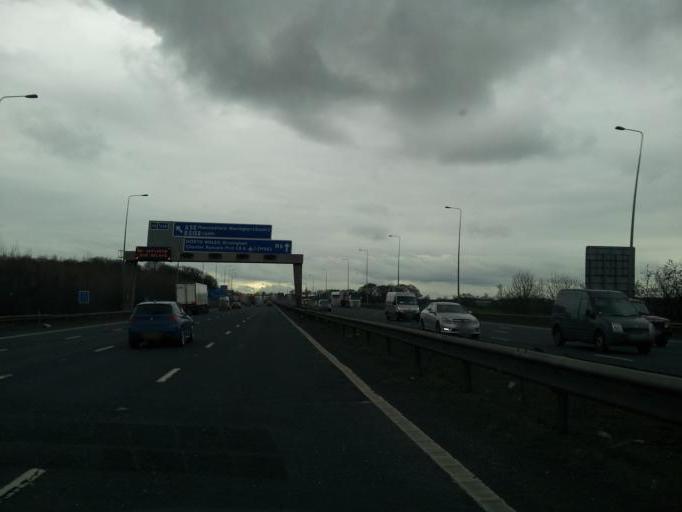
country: GB
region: England
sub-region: Warrington
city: Lymm
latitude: 53.3710
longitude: -2.5086
